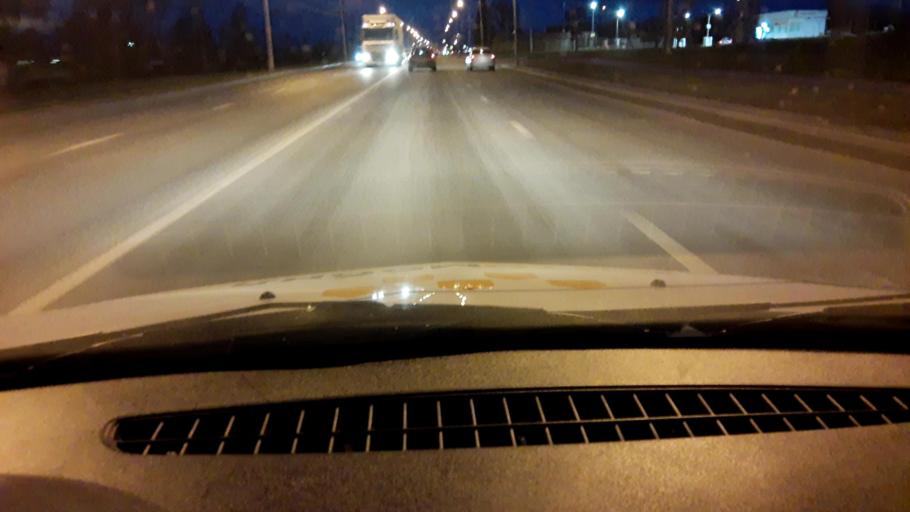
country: RU
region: Bashkortostan
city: Iglino
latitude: 54.7784
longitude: 56.2293
